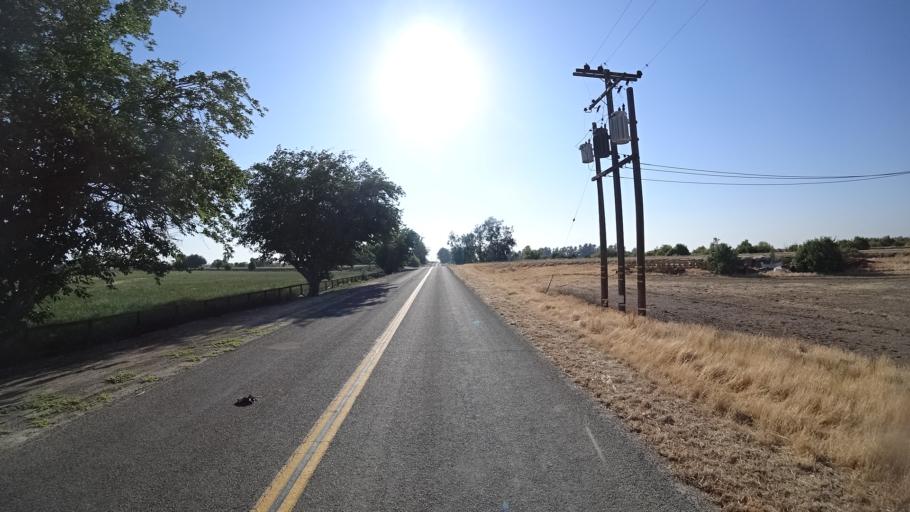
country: US
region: California
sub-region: Fresno County
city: Riverdale
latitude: 36.3765
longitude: -119.8862
